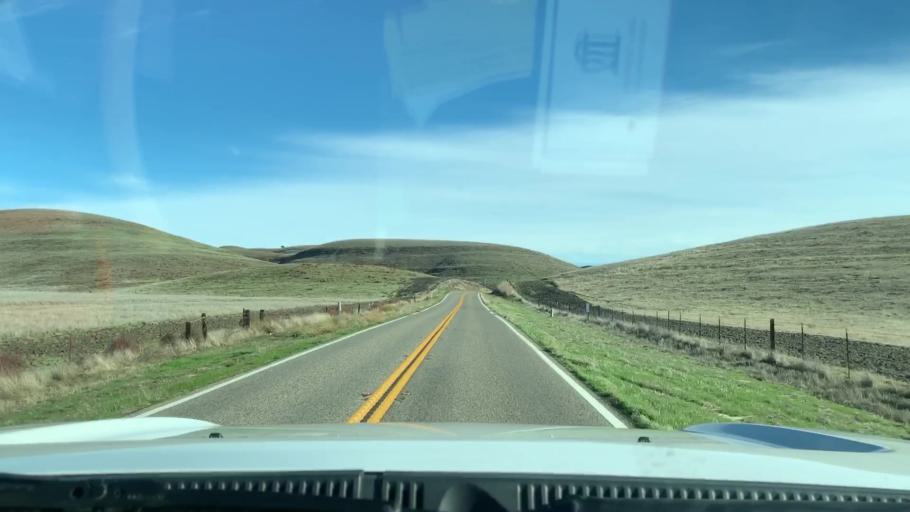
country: US
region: California
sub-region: Monterey County
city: King City
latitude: 36.1593
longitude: -120.9055
